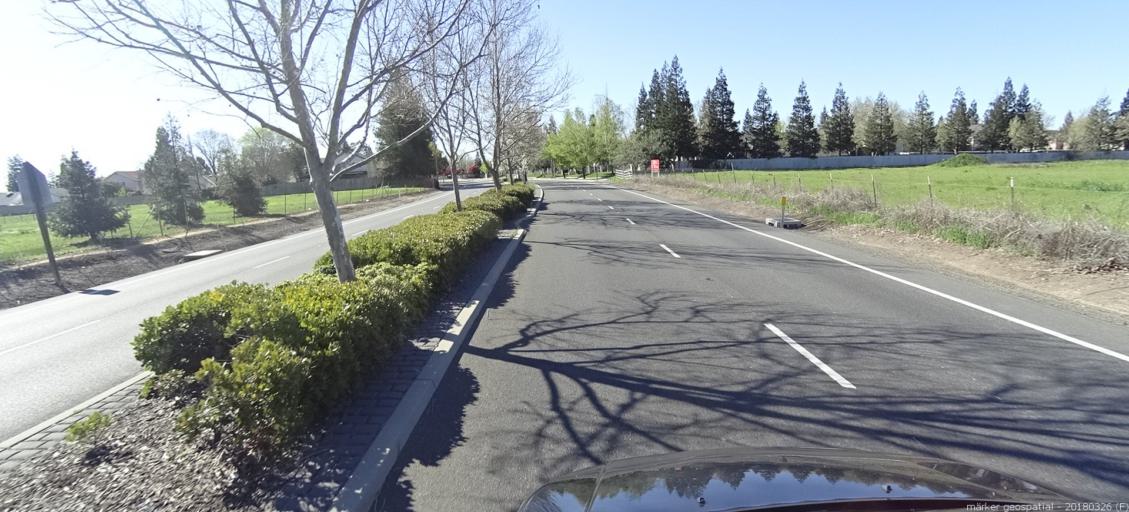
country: US
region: California
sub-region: Sacramento County
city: Florin
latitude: 38.4642
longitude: -121.4089
